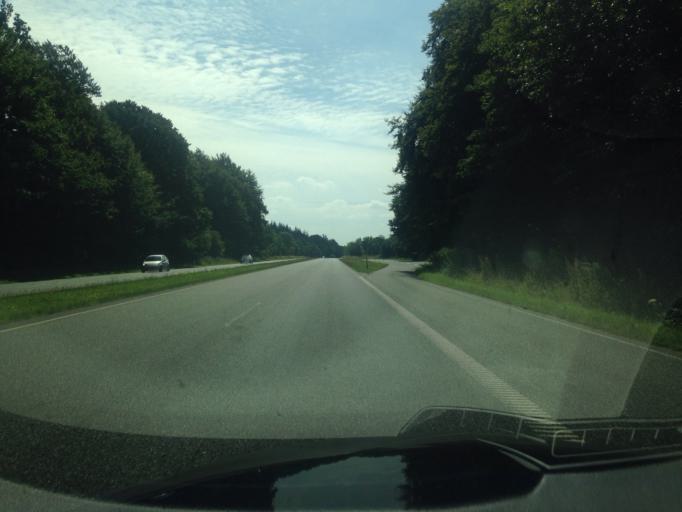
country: DK
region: South Denmark
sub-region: Kolding Kommune
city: Kolding
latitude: 55.5220
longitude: 9.4986
